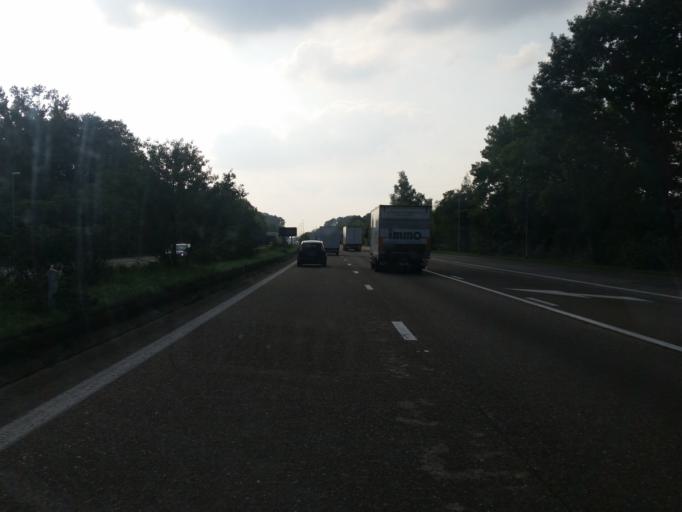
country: BE
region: Flanders
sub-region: Provincie Antwerpen
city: Oud-Turnhout
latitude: 51.2985
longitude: 4.9706
